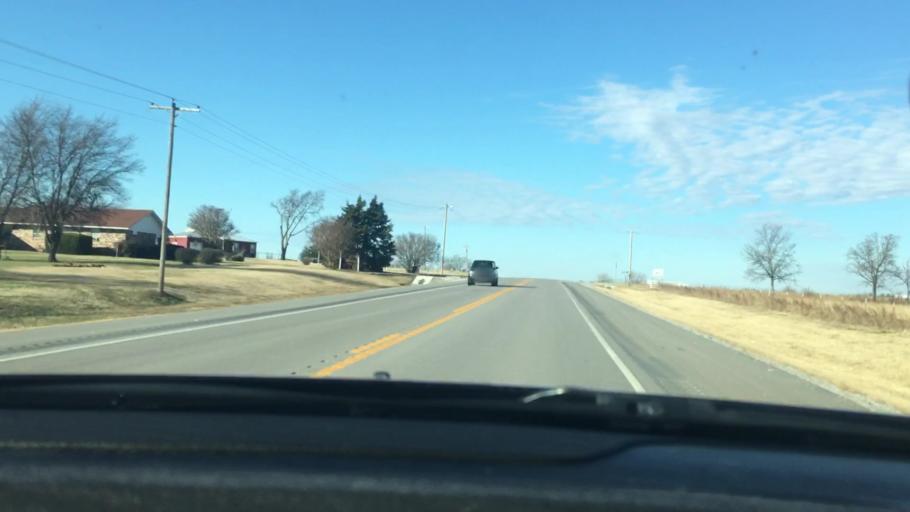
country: US
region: Oklahoma
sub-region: Love County
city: Marietta
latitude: 33.9404
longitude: -97.1853
